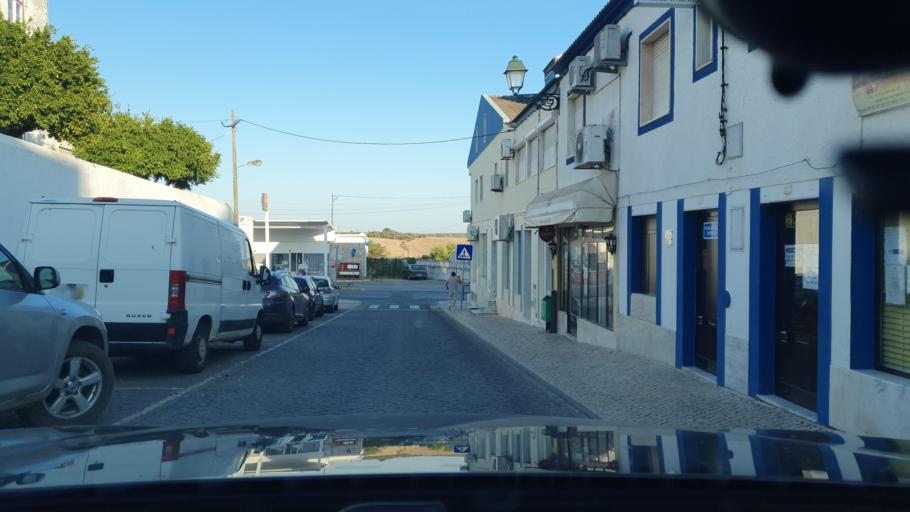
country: PT
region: Portalegre
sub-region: Fronteira
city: Fronteira
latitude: 38.9523
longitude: -7.6752
